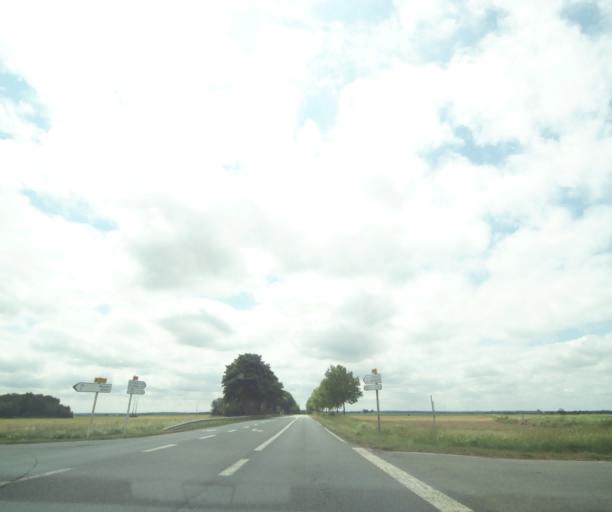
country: FR
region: Poitou-Charentes
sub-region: Departement des Deux-Sevres
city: Saint-Jean-de-Thouars
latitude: 46.9430
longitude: -0.2036
